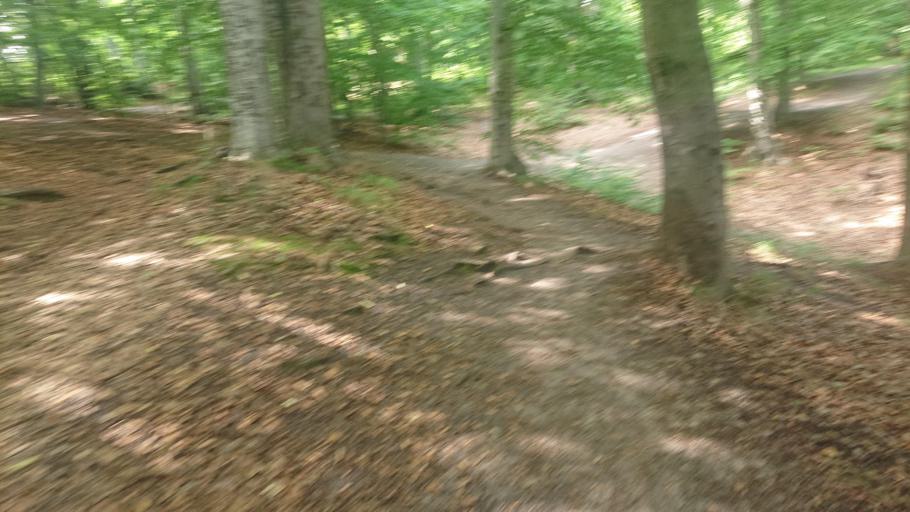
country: PL
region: Pomeranian Voivodeship
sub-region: Sopot
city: Sopot
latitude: 54.4684
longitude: 18.5617
